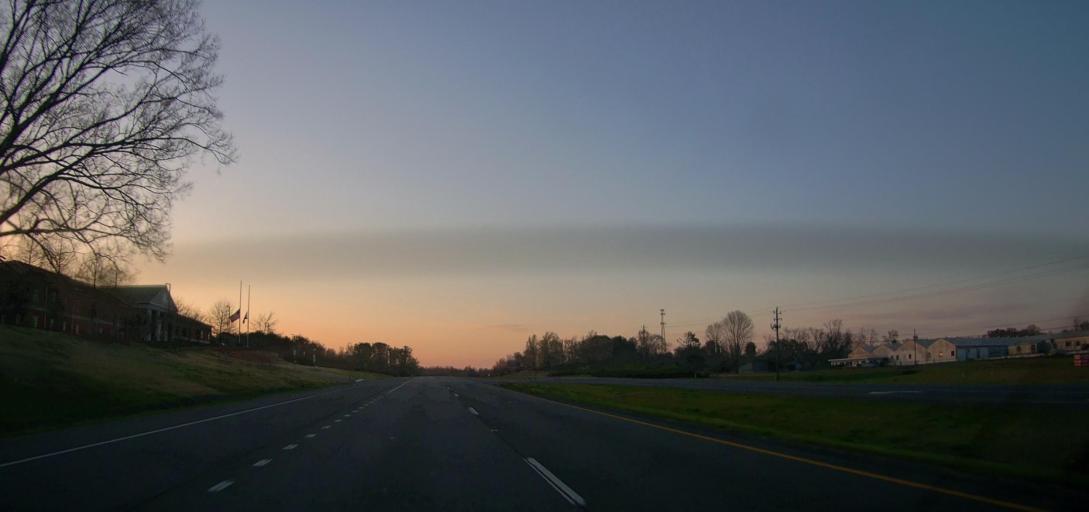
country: US
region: Alabama
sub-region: Tallapoosa County
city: Alexander City
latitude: 32.9629
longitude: -86.0049
